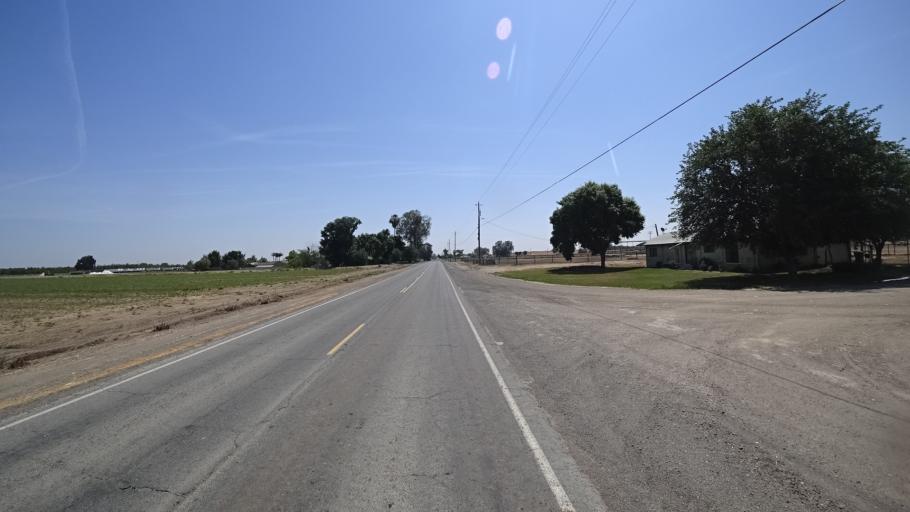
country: US
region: California
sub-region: Fresno County
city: Riverdale
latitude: 36.4021
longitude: -119.8179
